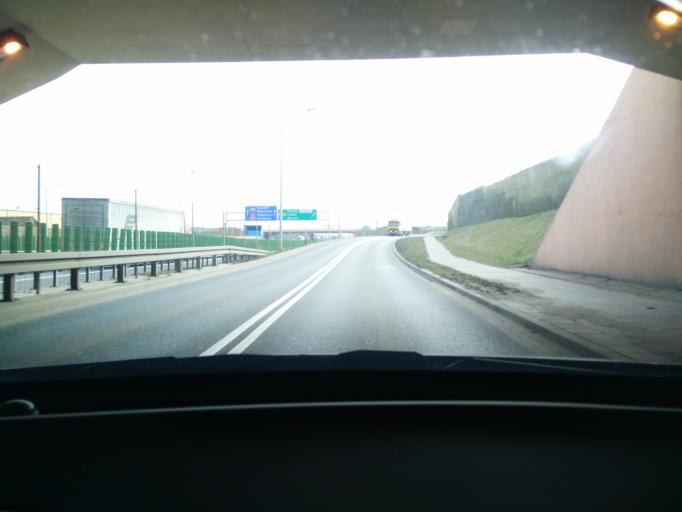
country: PL
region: Greater Poland Voivodeship
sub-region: Powiat poznanski
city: Lubon
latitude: 52.3541
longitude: 16.8963
